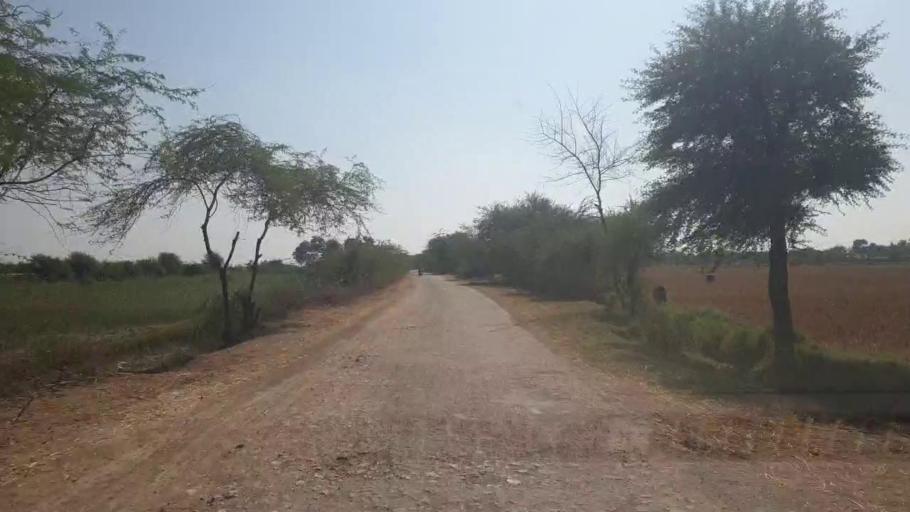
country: PK
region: Sindh
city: Badin
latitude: 24.6034
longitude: 68.8545
